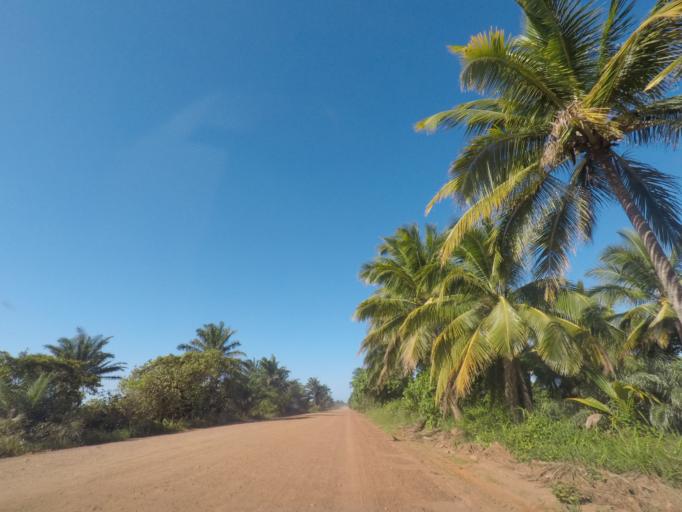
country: BR
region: Bahia
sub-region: Marau
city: Marau
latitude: -14.0594
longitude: -38.9570
